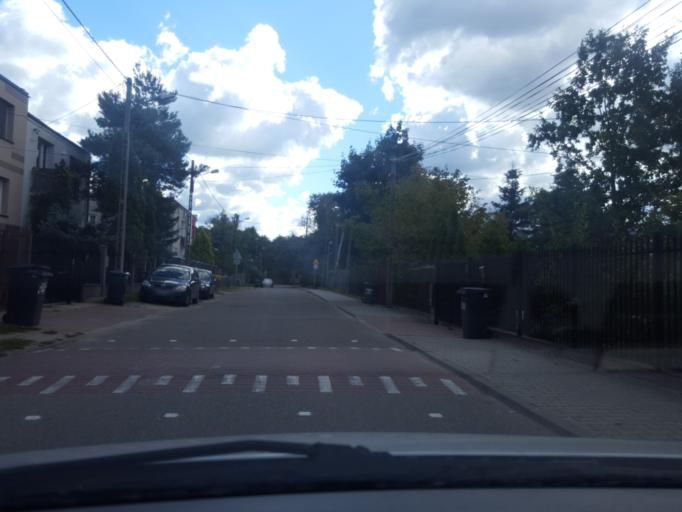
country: PL
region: Masovian Voivodeship
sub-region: Warszawa
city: Rembertow
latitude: 52.2691
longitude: 21.1682
